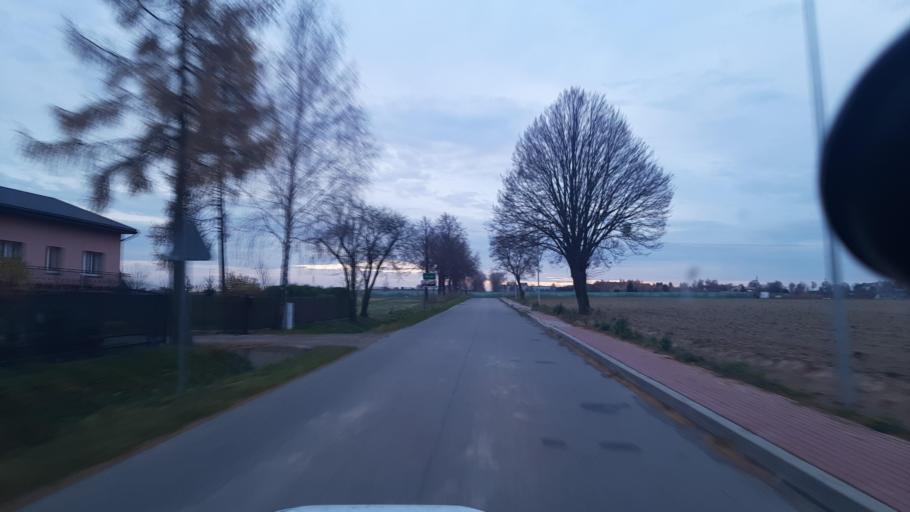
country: PL
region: Lublin Voivodeship
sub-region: Powiat lubelski
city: Garbow
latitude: 51.3540
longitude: 22.3695
